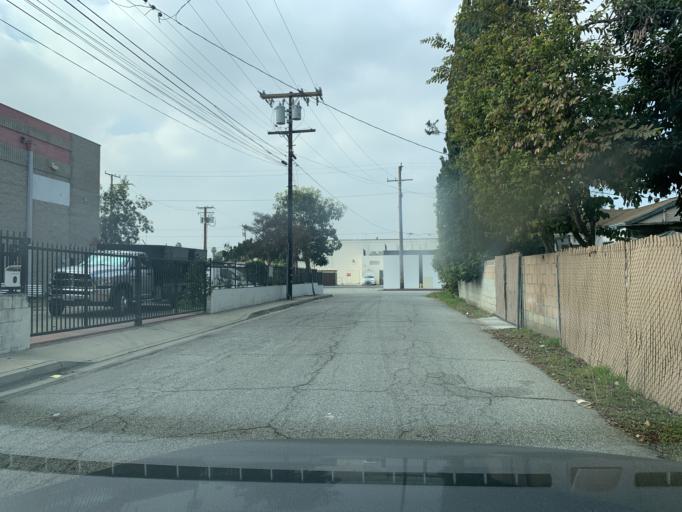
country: US
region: California
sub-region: Los Angeles County
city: South El Monte
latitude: 34.0618
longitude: -118.0508
